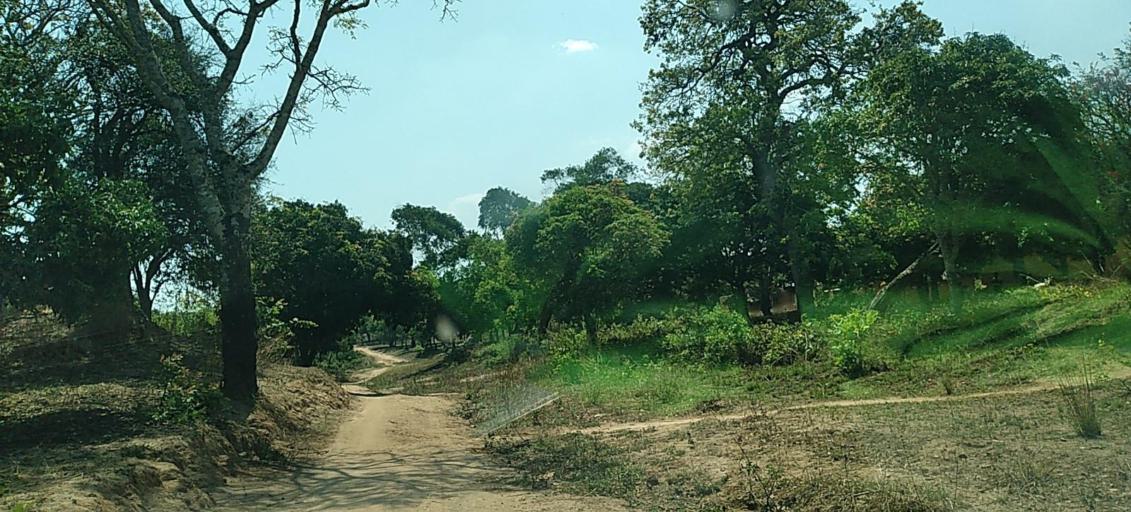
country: CD
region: Katanga
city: Kolwezi
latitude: -11.2822
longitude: 25.1475
